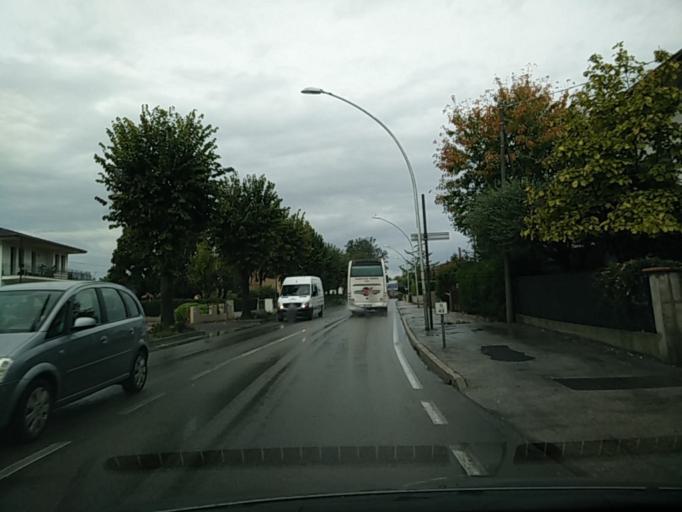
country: IT
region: Veneto
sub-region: Provincia di Vicenza
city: Rossano Veneto
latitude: 45.6963
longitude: 11.8312
